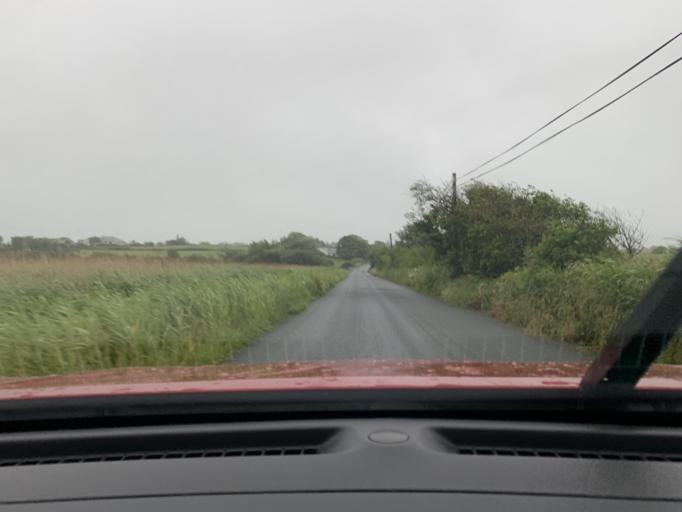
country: IE
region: Connaught
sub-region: County Leitrim
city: Kinlough
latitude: 54.4454
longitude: -8.4428
